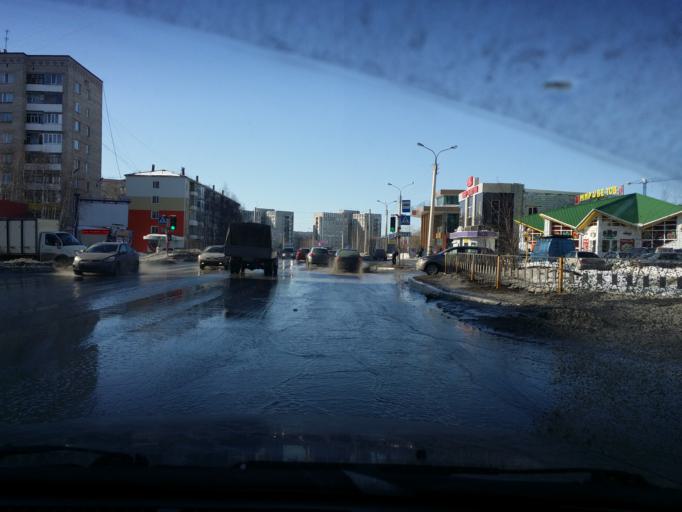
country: RU
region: Khanty-Mansiyskiy Avtonomnyy Okrug
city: Nizhnevartovsk
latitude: 60.9447
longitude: 76.5725
